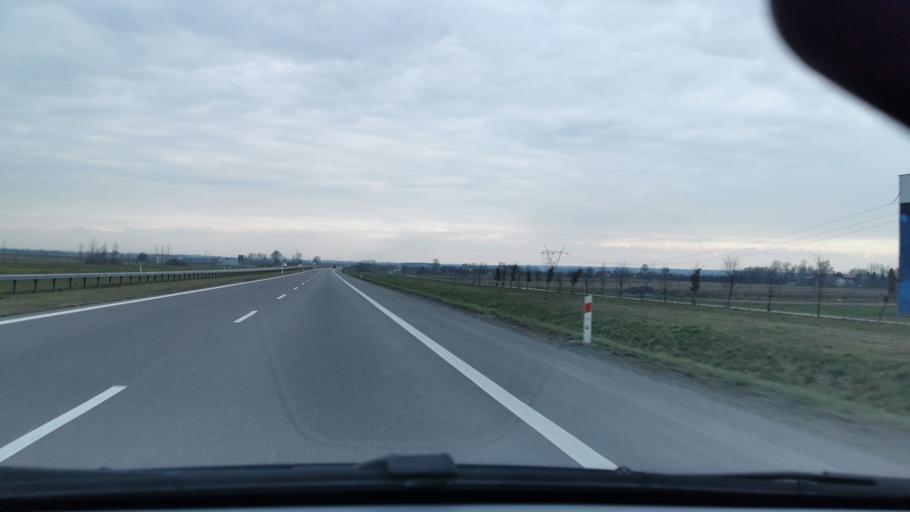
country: PL
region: Lublin Voivodeship
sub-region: Powiat pulawski
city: Markuszow
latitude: 51.3918
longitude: 22.2380
